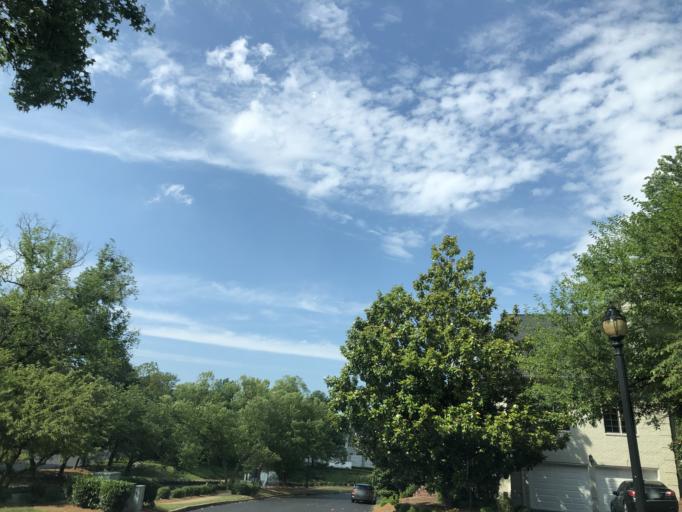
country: US
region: Tennessee
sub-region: Davidson County
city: Belle Meade
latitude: 36.1279
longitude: -86.8217
